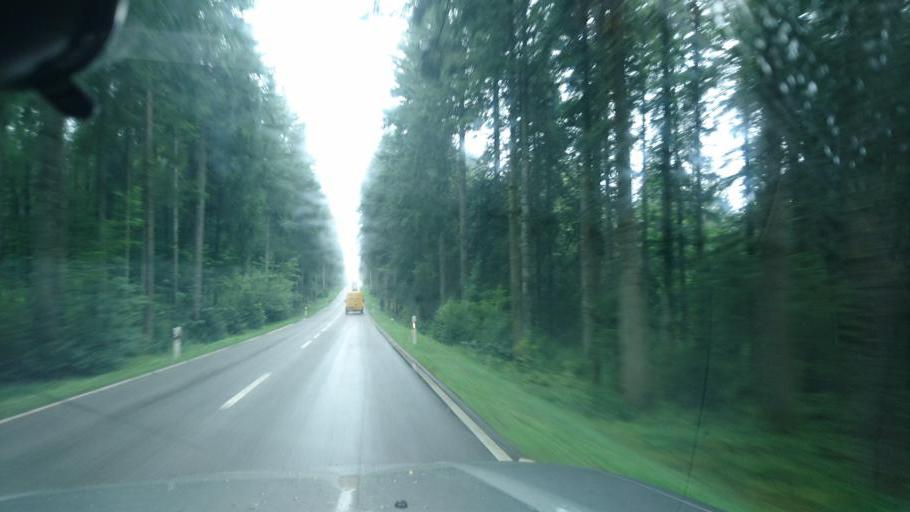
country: DE
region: Baden-Wuerttemberg
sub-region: Karlsruhe Region
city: Baiersbronn
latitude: 48.5760
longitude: 8.4240
